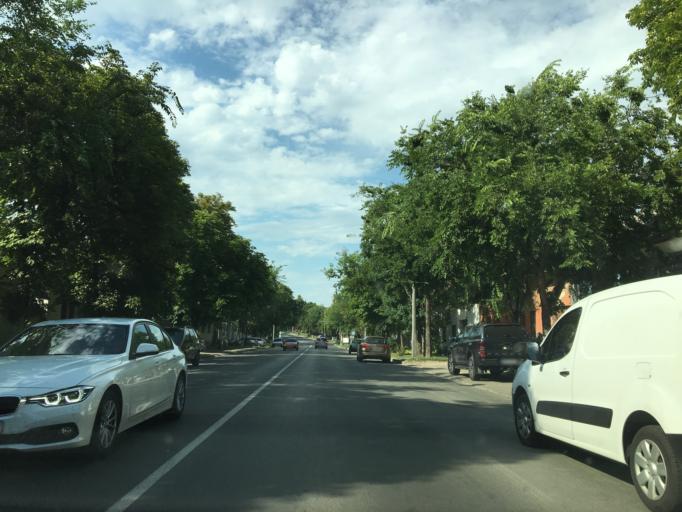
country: HU
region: Tolna
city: Szekszard
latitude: 46.3542
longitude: 18.7035
